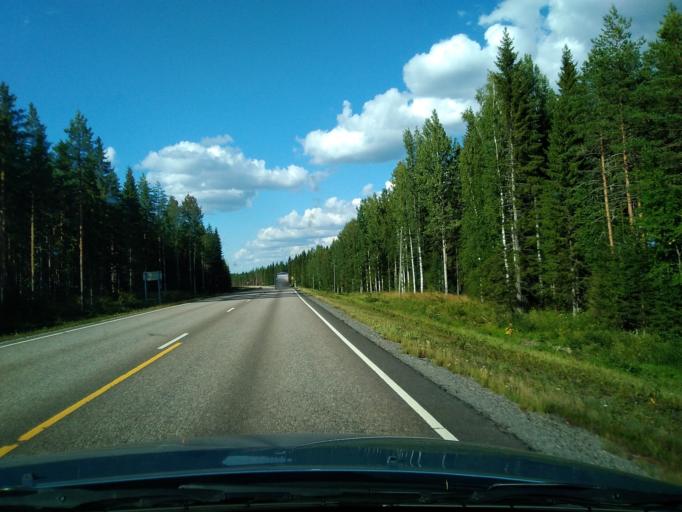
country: FI
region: Pirkanmaa
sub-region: Ylae-Pirkanmaa
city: Maenttae
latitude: 62.0835
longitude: 24.7269
